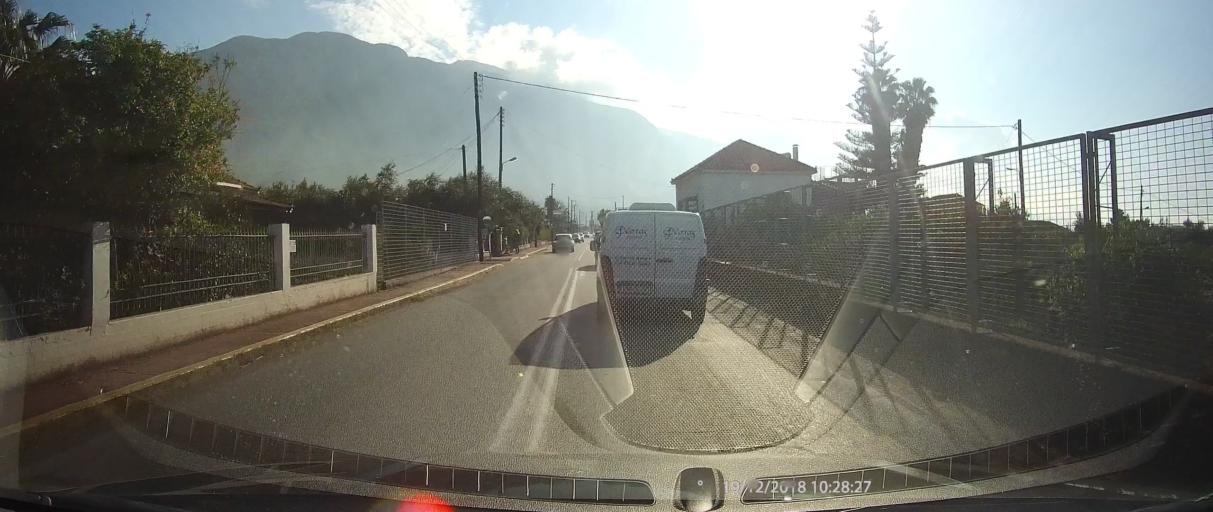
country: GR
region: Peloponnese
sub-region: Nomos Messinias
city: Paralia Vergas
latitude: 37.0280
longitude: 22.1411
